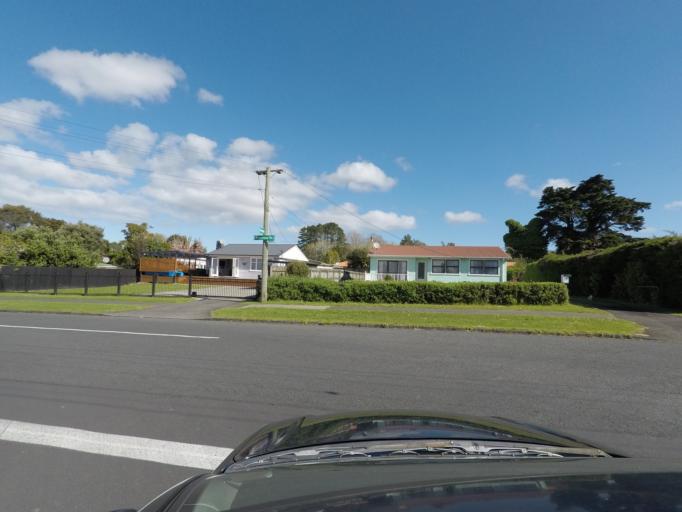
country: NZ
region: Auckland
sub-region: Auckland
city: Rosebank
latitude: -36.8665
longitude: 174.6014
